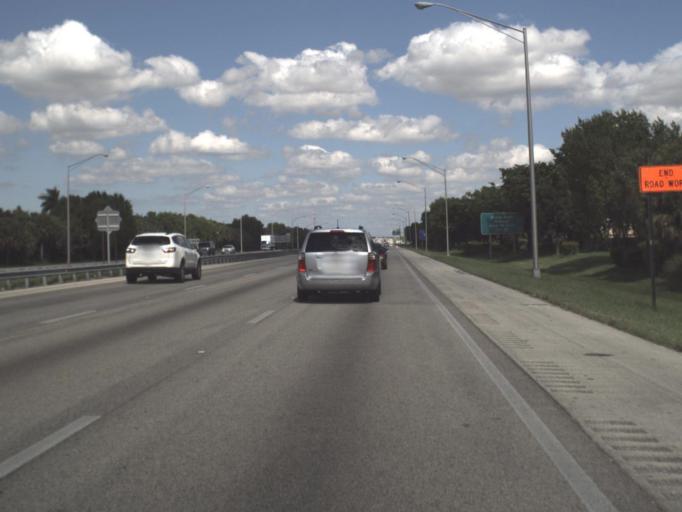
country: US
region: Florida
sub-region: Miami-Dade County
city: The Crossings
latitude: 25.6737
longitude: -80.3885
